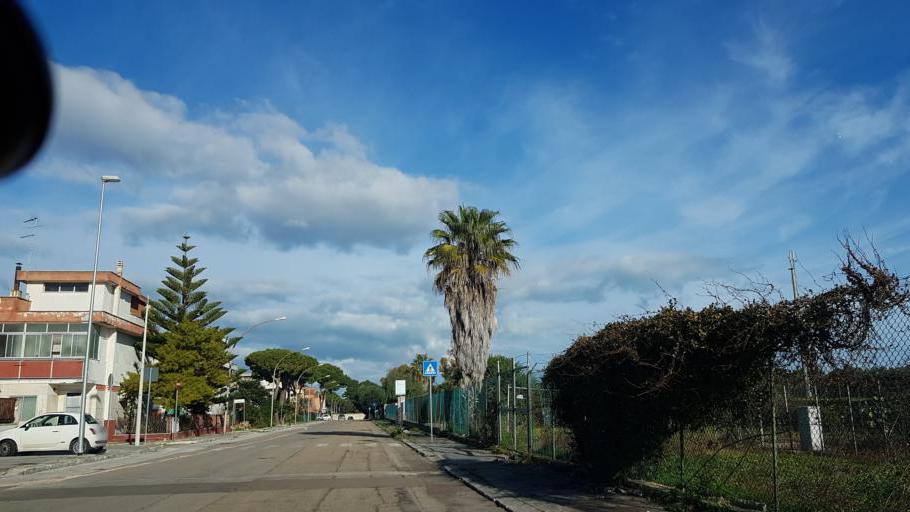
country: IT
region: Apulia
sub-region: Provincia di Brindisi
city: La Rosa
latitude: 40.6070
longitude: 17.9536
